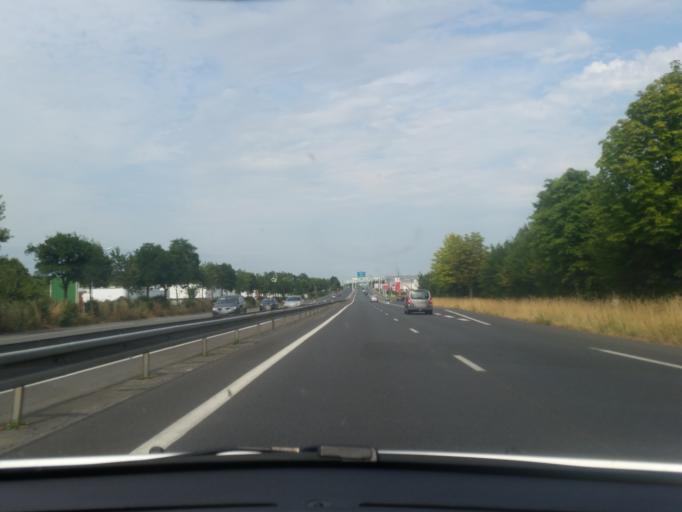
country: FR
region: Pays de la Loire
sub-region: Departement de Maine-et-Loire
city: Beaucouze
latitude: 47.4655
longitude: -0.6328
